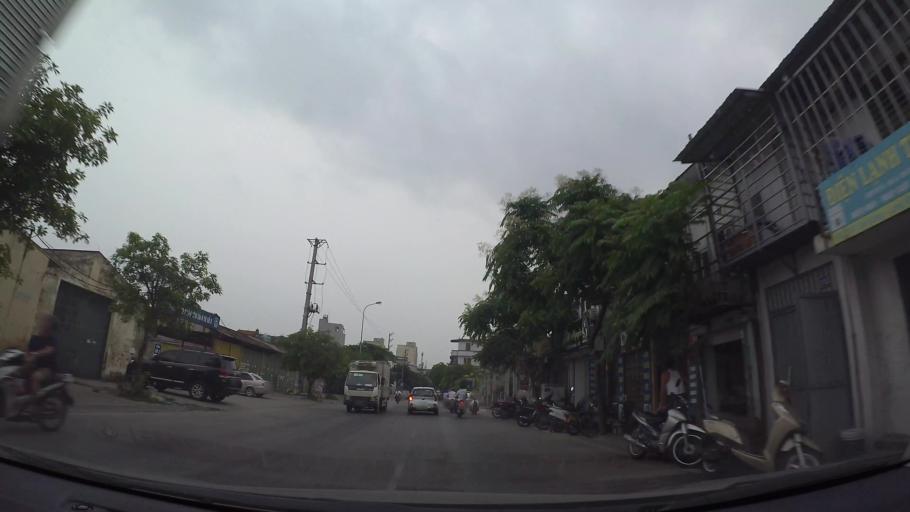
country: VN
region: Ha Noi
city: Trau Quy
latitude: 21.0379
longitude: 105.9121
